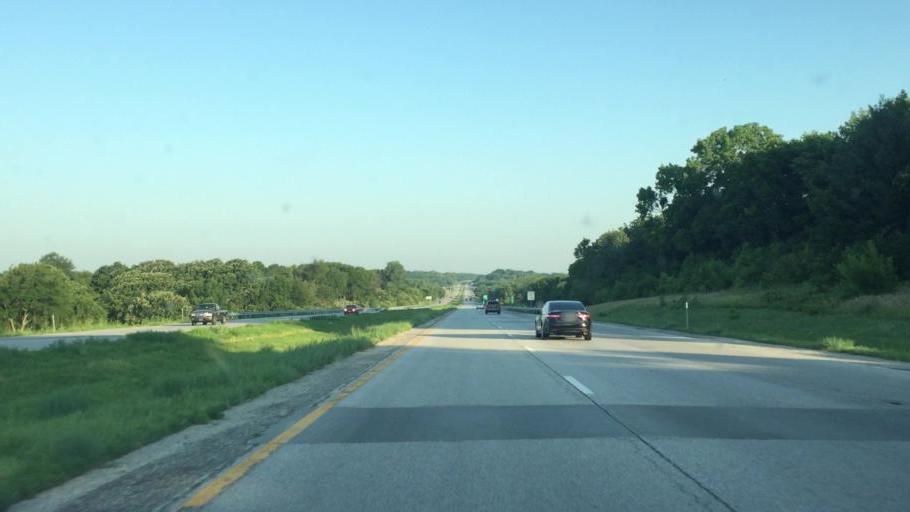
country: US
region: Missouri
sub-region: Buchanan County
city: Saint Joseph
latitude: 39.7112
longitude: -94.8005
